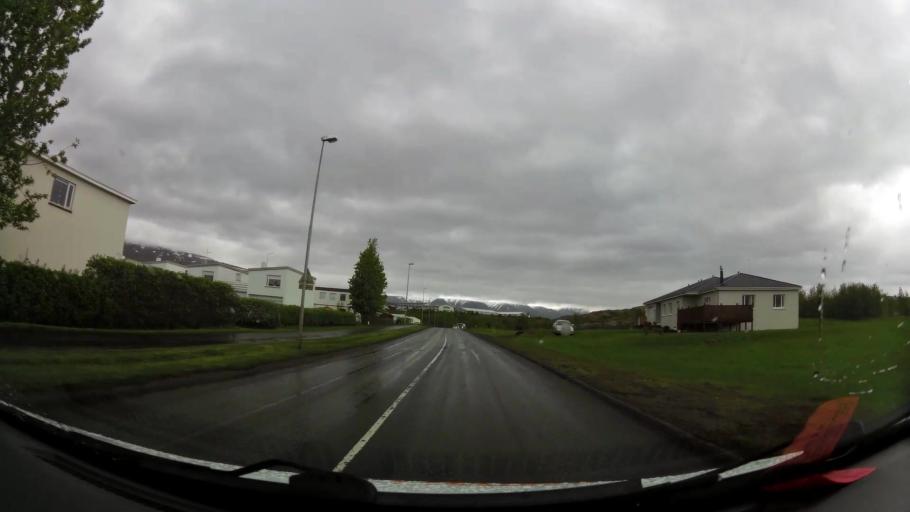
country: IS
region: Northeast
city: Akureyri
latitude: 65.6954
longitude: -18.1111
